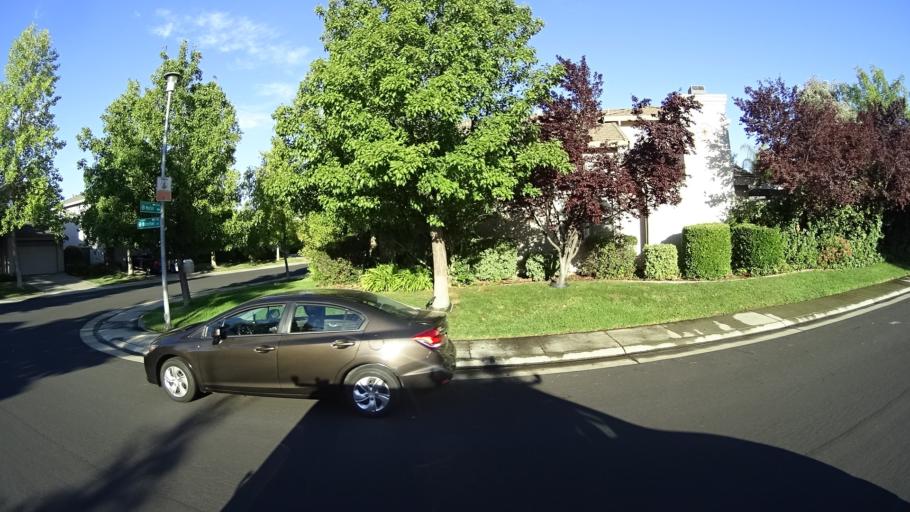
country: US
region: California
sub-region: Sacramento County
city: Laguna
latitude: 38.4043
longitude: -121.4766
